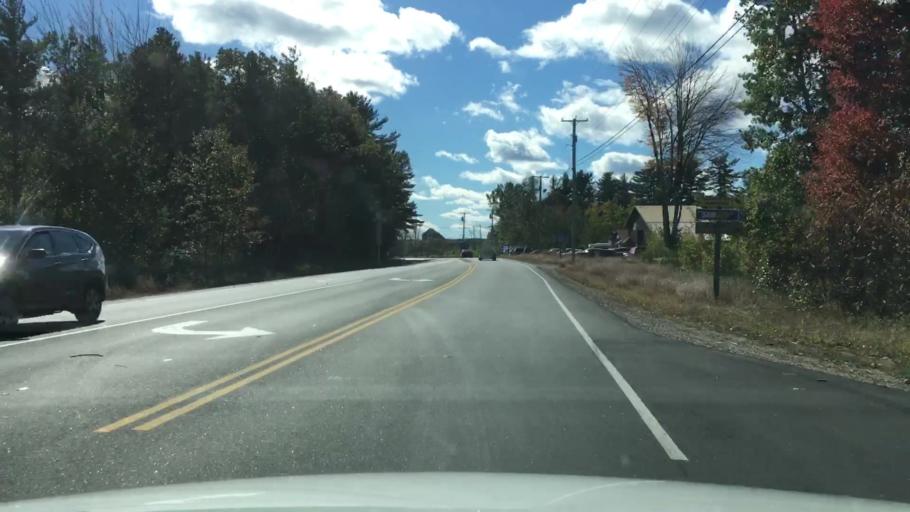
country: US
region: Maine
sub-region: York County
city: South Sanford
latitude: 43.4161
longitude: -70.7407
